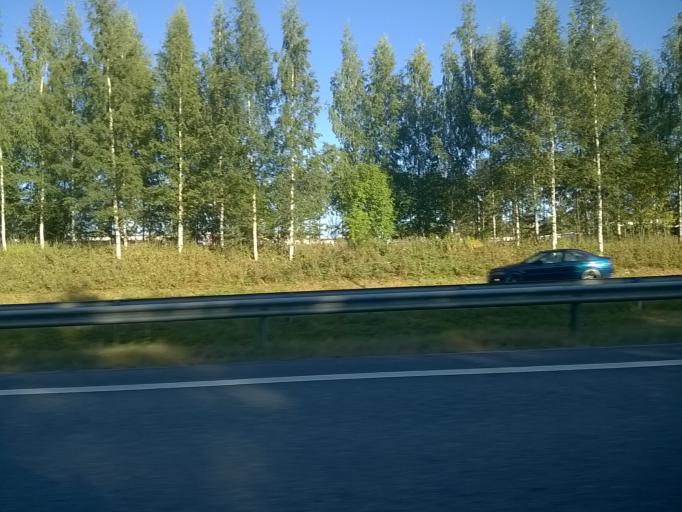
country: FI
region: Pirkanmaa
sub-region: Tampere
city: Tampere
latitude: 61.4760
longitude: 23.8691
